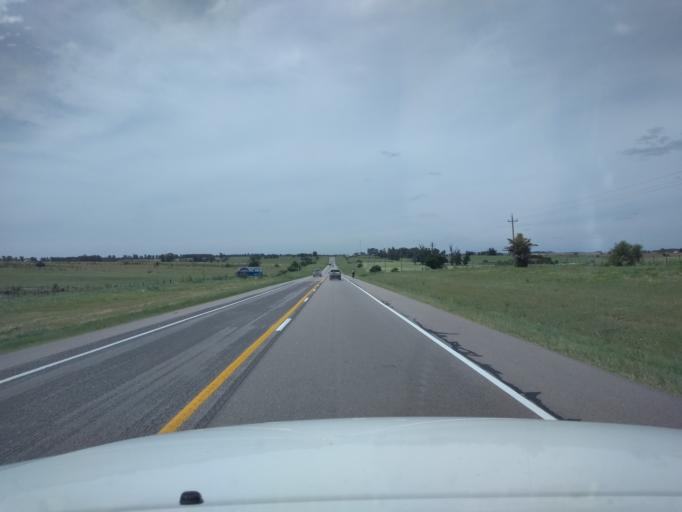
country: UY
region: Florida
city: Florida
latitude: -34.2243
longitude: -56.2103
